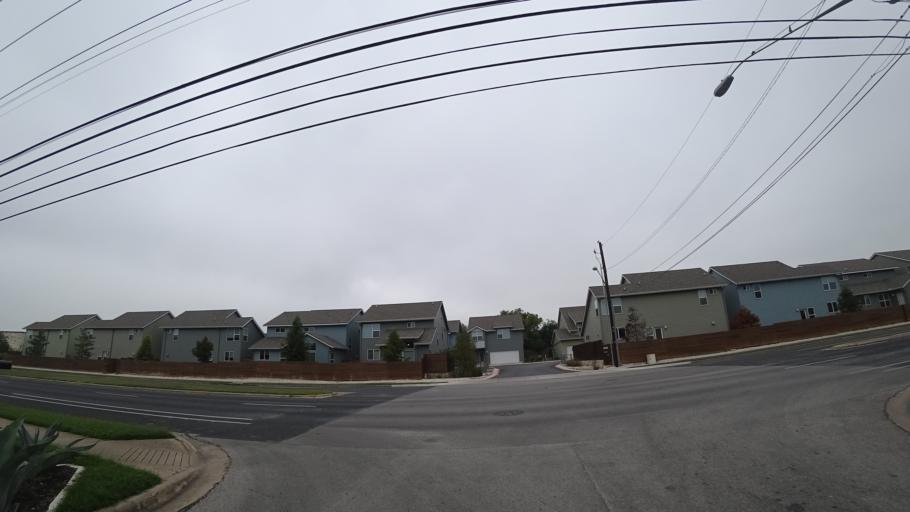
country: US
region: Texas
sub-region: Travis County
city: Austin
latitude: 30.2064
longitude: -97.7772
